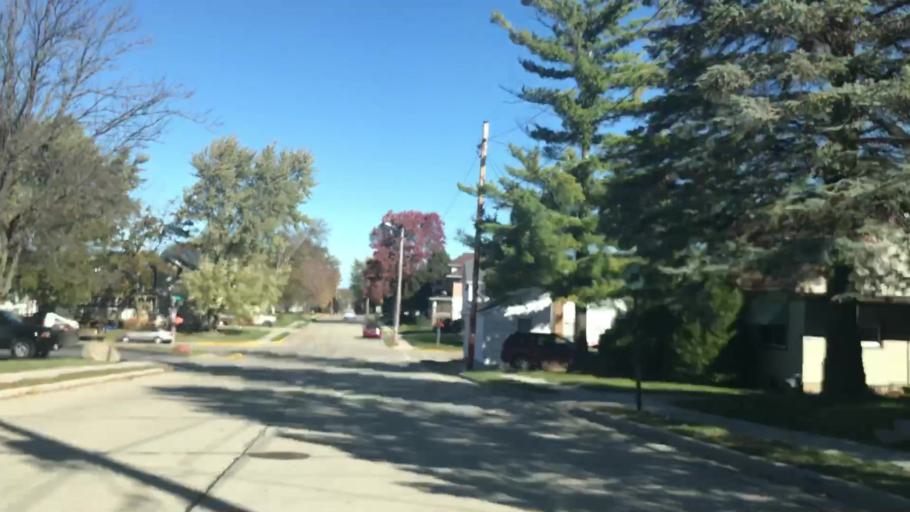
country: US
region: Wisconsin
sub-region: Dodge County
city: Mayville
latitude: 43.4950
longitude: -88.5525
